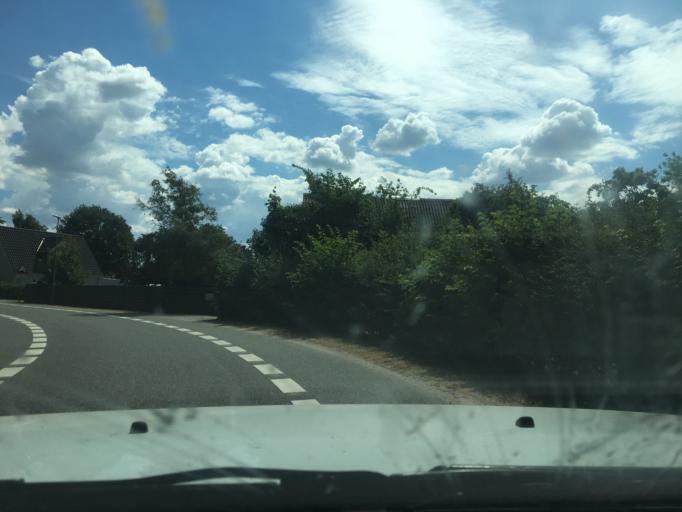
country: DK
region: Central Jutland
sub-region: Syddjurs Kommune
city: Hornslet
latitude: 56.3484
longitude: 10.2886
